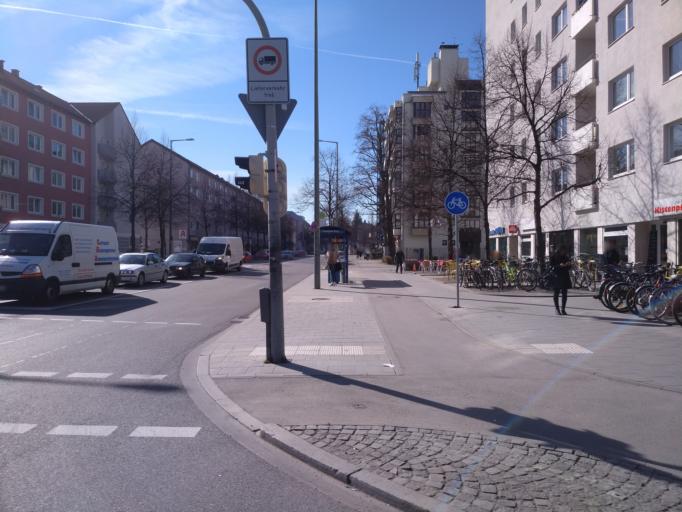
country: DE
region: Bavaria
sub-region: Upper Bavaria
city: Munich
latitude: 48.1874
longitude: 11.5725
